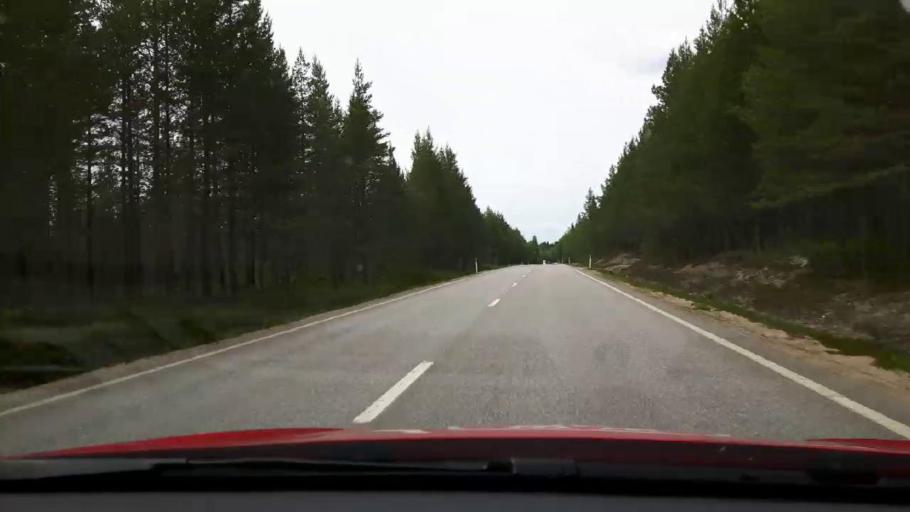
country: SE
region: Jaemtland
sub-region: Harjedalens Kommun
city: Sveg
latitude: 62.0606
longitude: 14.2871
